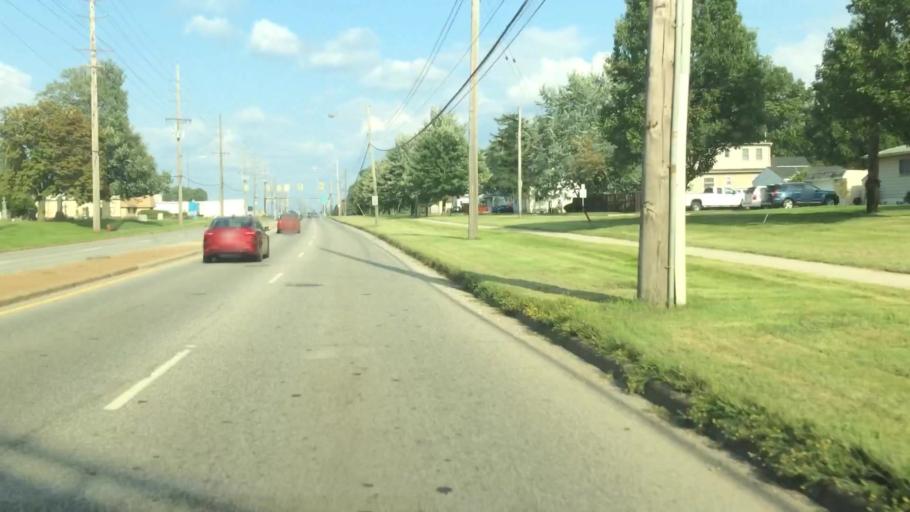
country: US
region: Ohio
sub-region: Cuyahoga County
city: Brook Park
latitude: 41.4184
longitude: -81.8018
